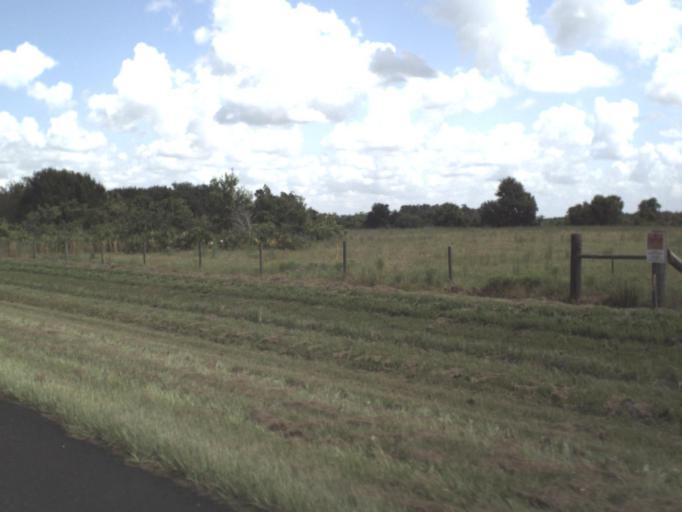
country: US
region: Florida
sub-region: Hardee County
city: Zolfo Springs
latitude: 27.4272
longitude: -81.7958
